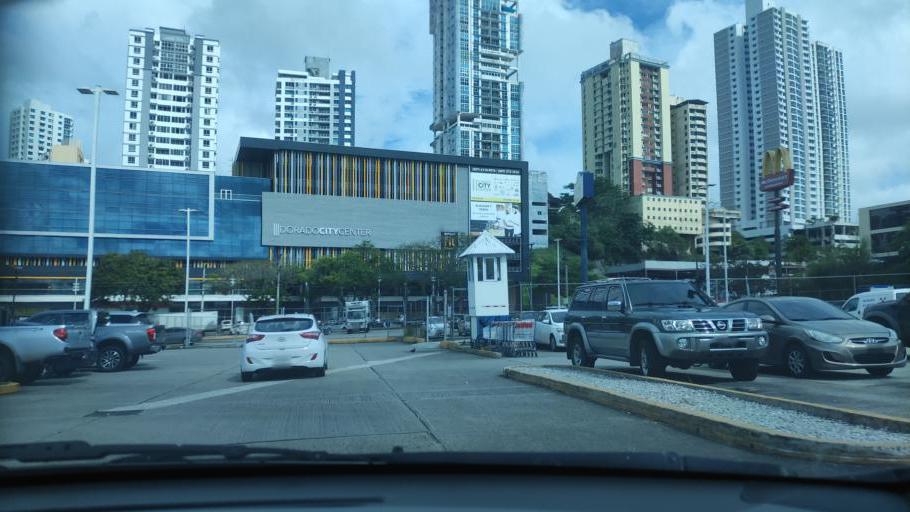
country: PA
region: Panama
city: Panama
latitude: 9.0151
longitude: -79.5361
